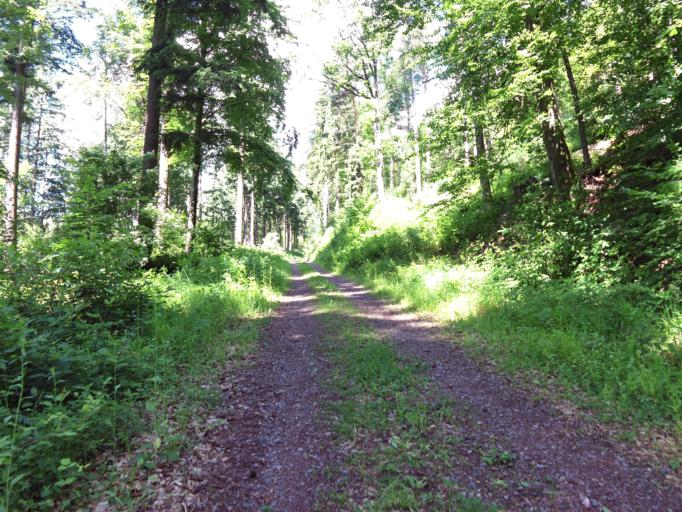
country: DE
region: Rheinland-Pfalz
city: Sankt Martin
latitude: 49.2957
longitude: 8.0521
